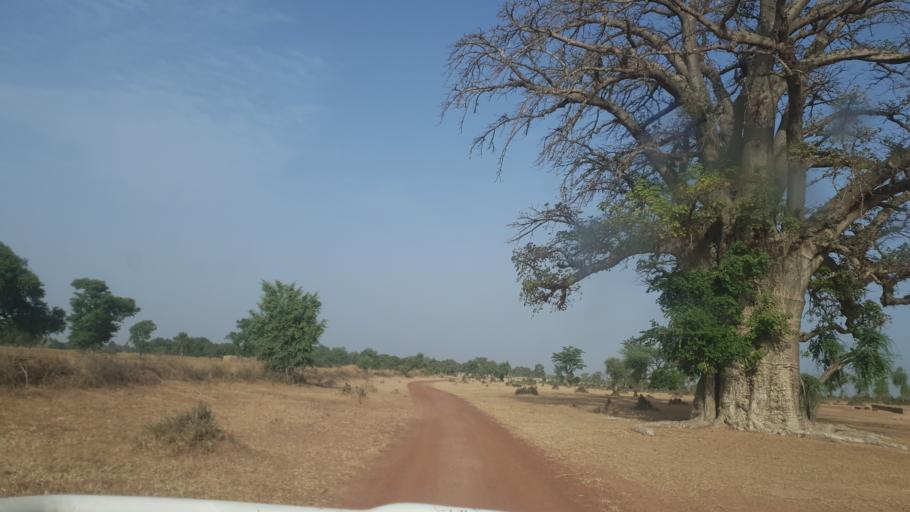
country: ML
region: Segou
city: Baroueli
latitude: 13.3559
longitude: -6.9265
